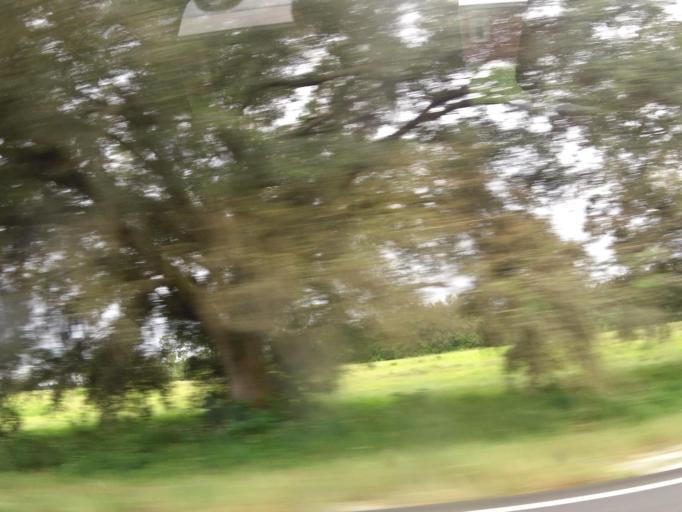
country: US
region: Florida
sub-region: Baker County
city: Macclenny
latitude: 30.3915
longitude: -82.1794
